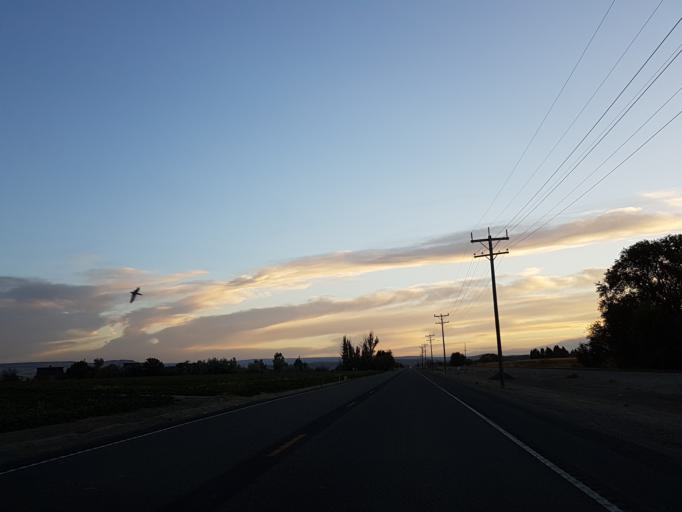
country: US
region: Oregon
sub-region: Malheur County
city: Vale
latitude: 43.9712
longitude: -117.2670
